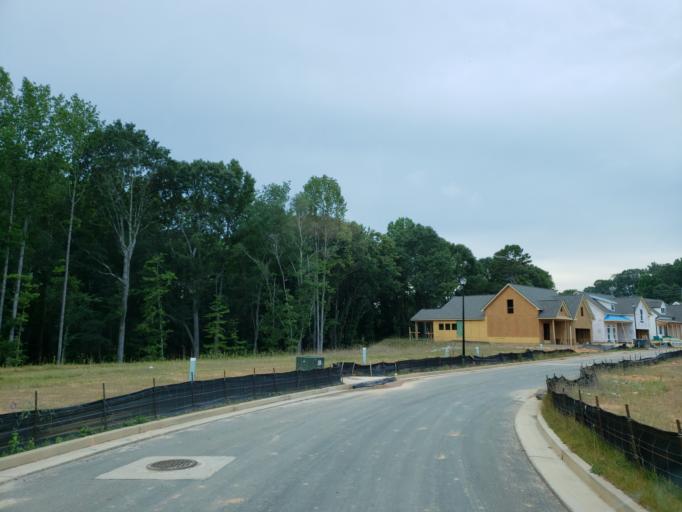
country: US
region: Georgia
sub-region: Cherokee County
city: Holly Springs
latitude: 34.1792
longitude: -84.4360
